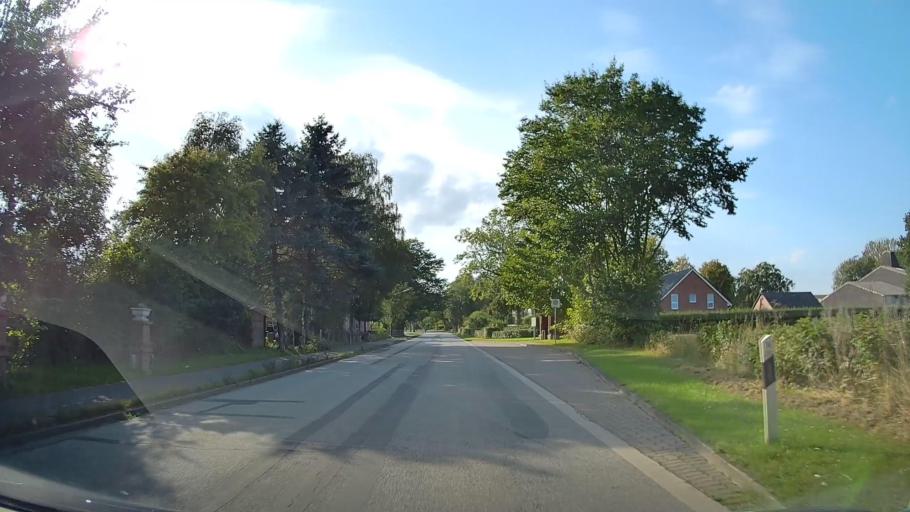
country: DE
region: Schleswig-Holstein
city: Riepsdorf
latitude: 54.1957
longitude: 10.9960
